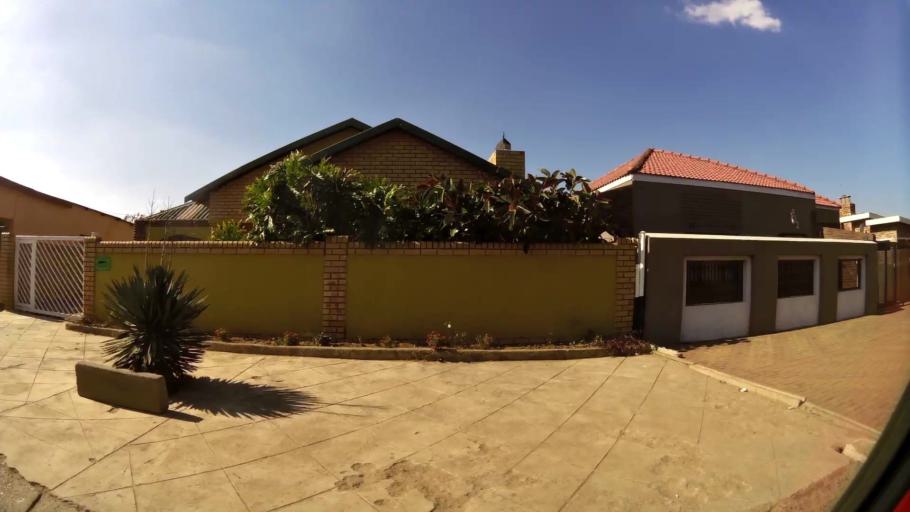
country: ZA
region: Gauteng
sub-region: City of Johannesburg Metropolitan Municipality
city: Soweto
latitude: -26.2390
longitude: 27.8853
